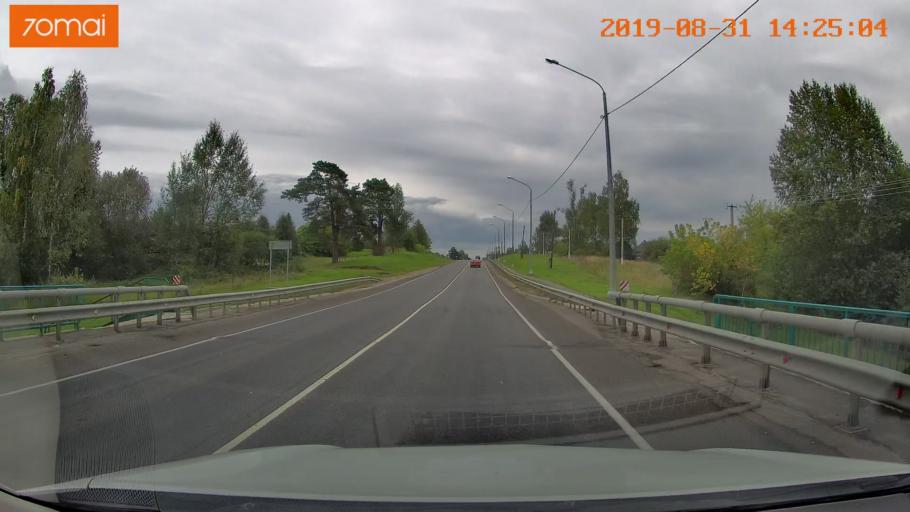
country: RU
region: Smolensk
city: Yekimovichi
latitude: 54.1064
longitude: 33.2667
